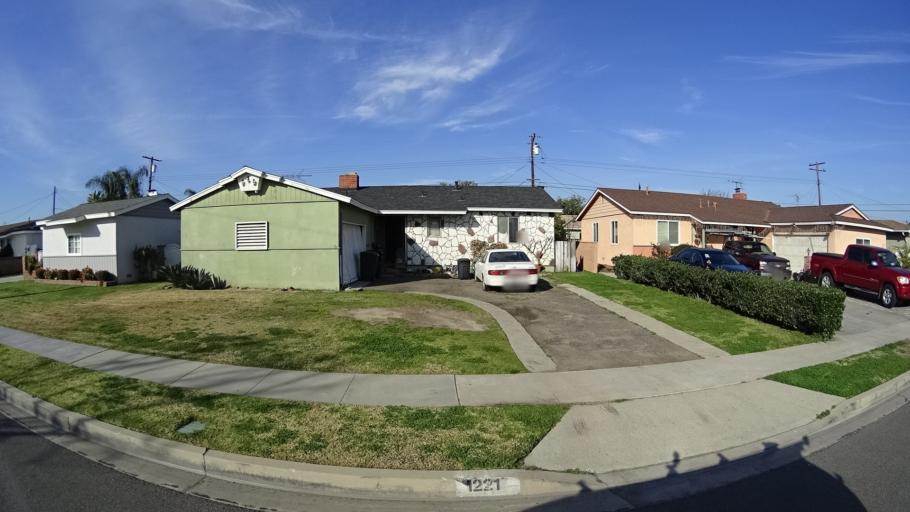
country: US
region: California
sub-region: Orange County
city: Fullerton
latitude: 33.8516
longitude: -117.9253
